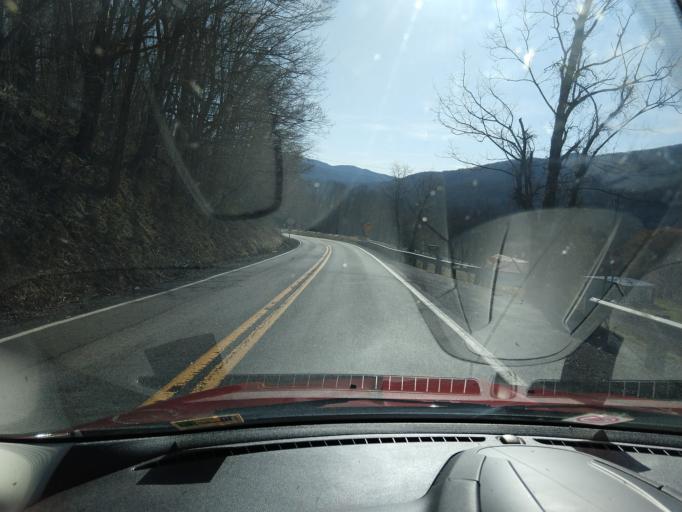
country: US
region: West Virginia
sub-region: Summers County
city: Hinton
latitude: 37.7667
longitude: -80.8902
